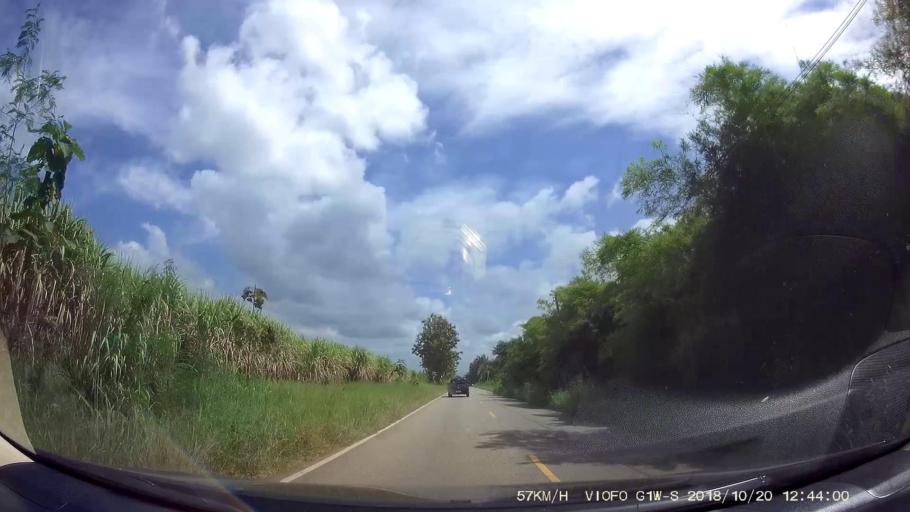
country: TH
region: Chaiyaphum
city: Khon San
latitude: 16.5403
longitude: 101.8653
